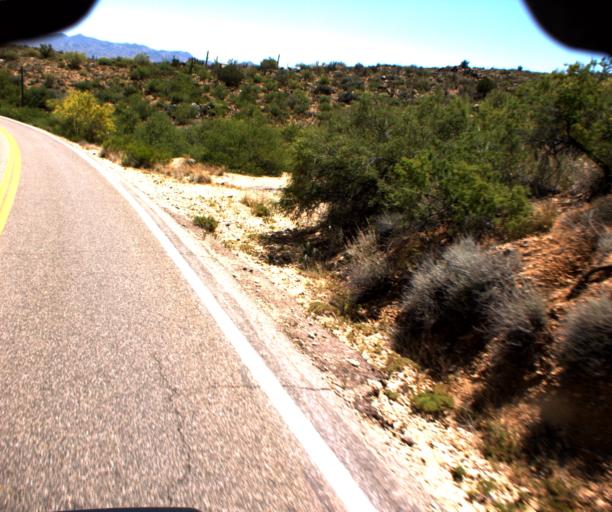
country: US
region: Arizona
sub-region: Yavapai County
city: Bagdad
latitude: 34.5232
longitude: -113.1152
